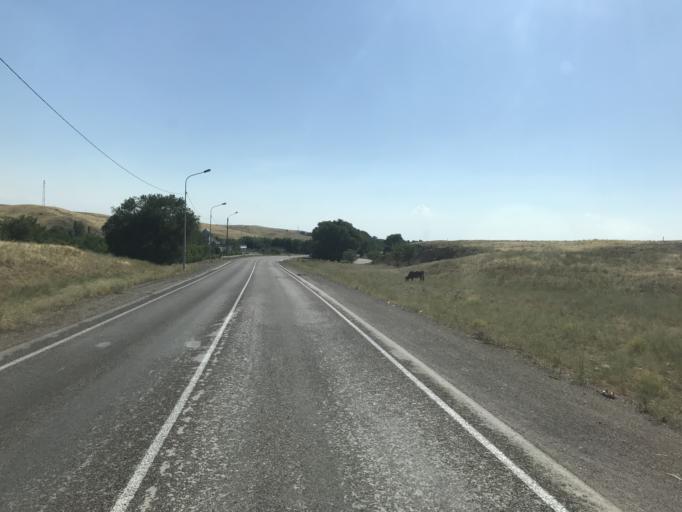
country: KZ
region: Zhambyl
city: Georgiyevka
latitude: 43.2424
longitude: 74.7790
